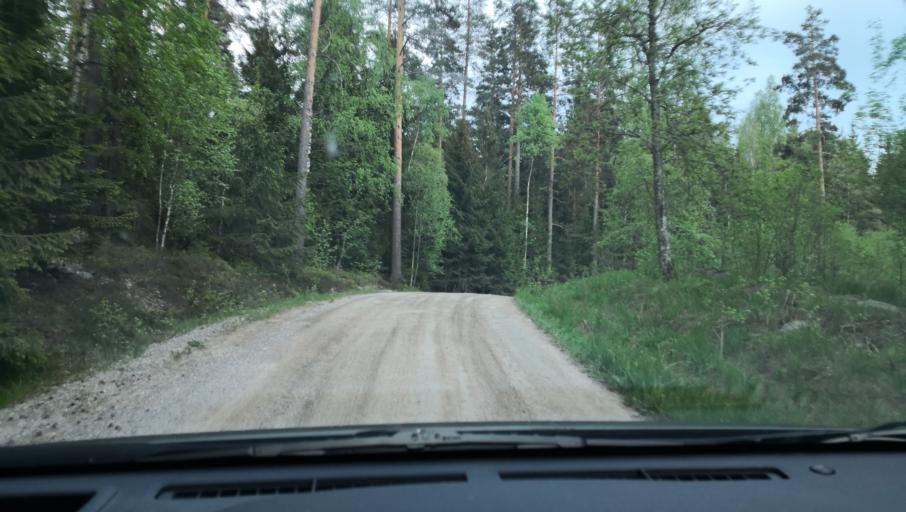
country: SE
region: Vaestmanland
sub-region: Skinnskattebergs Kommun
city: Skinnskatteberg
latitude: 59.7311
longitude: 15.4753
